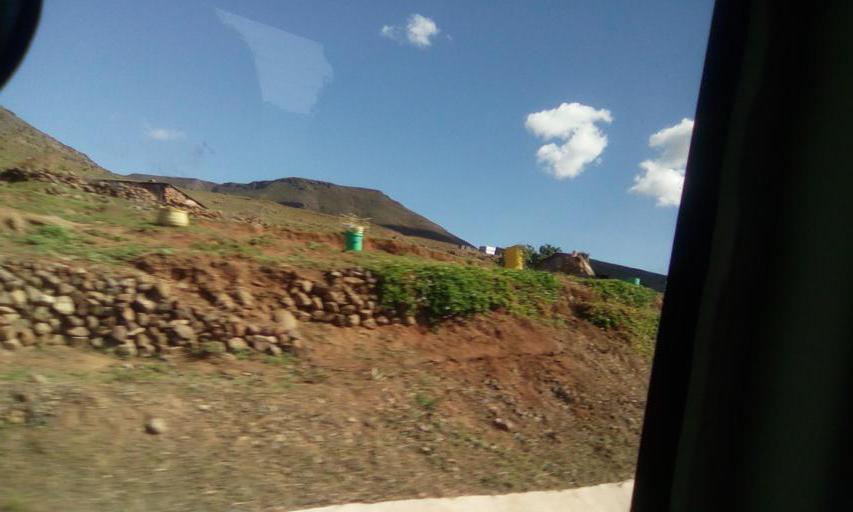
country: LS
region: Qacha's Nek
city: Qacha's Nek
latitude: -30.0209
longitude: 28.1734
